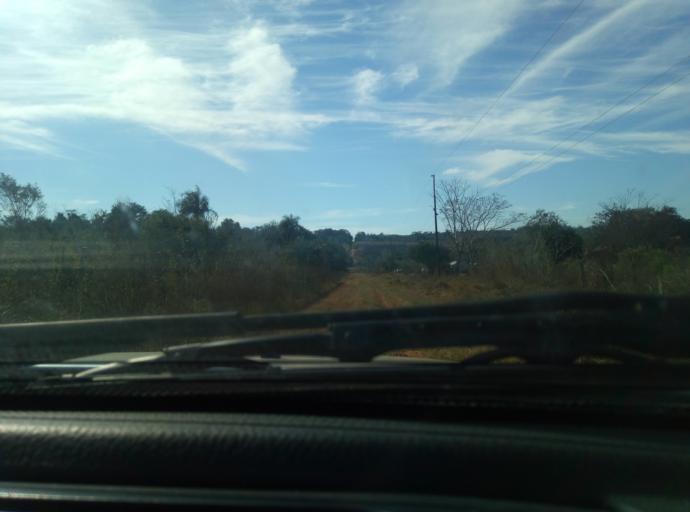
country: PY
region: Caaguazu
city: Carayao
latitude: -25.1695
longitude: -56.2931
